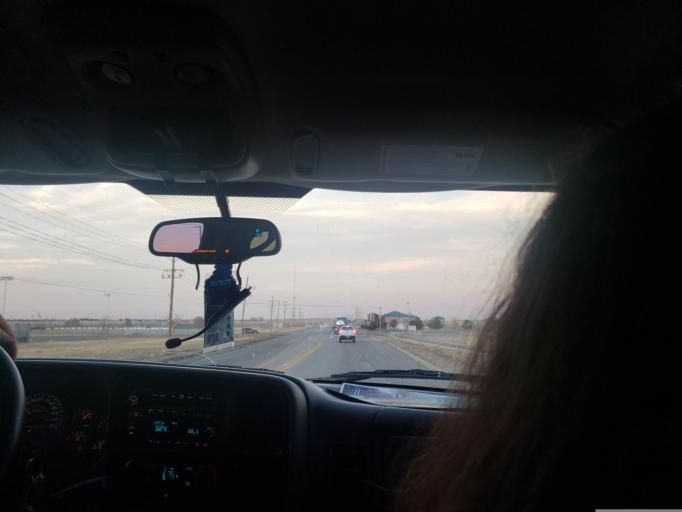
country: US
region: Kansas
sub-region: Seward County
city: Liberal
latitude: 37.0502
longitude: -100.9042
